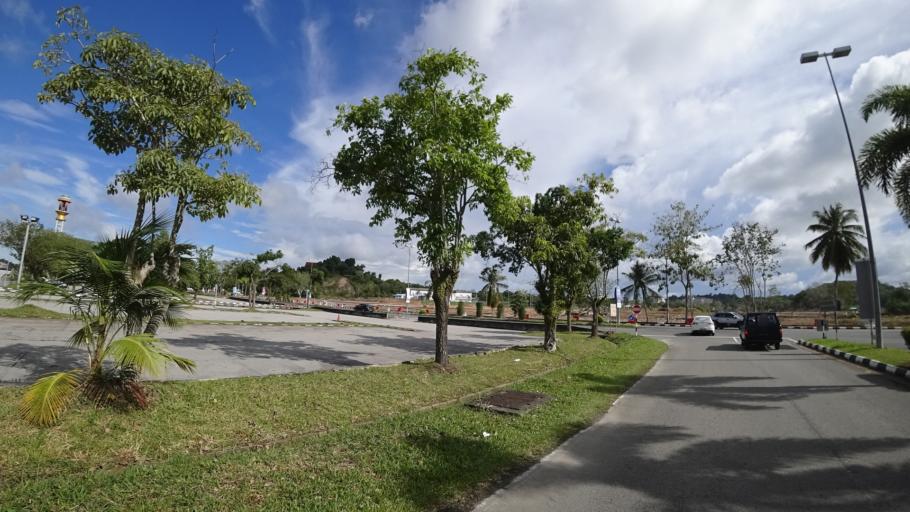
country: BN
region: Brunei and Muara
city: Bandar Seri Begawan
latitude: 4.9276
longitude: 114.9438
